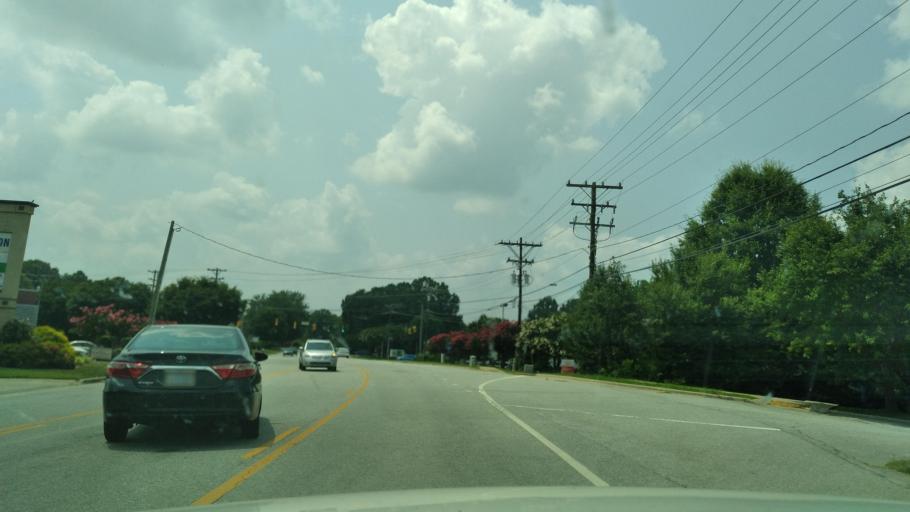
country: US
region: North Carolina
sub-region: Guilford County
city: Summerfield
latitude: 36.1259
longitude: -79.9051
